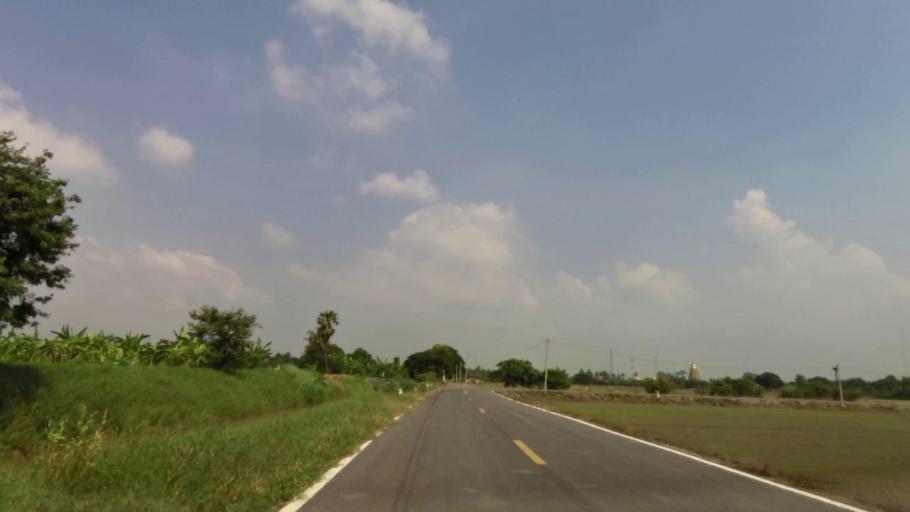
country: TH
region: Ang Thong
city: Pho Thong
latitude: 14.6284
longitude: 100.4054
